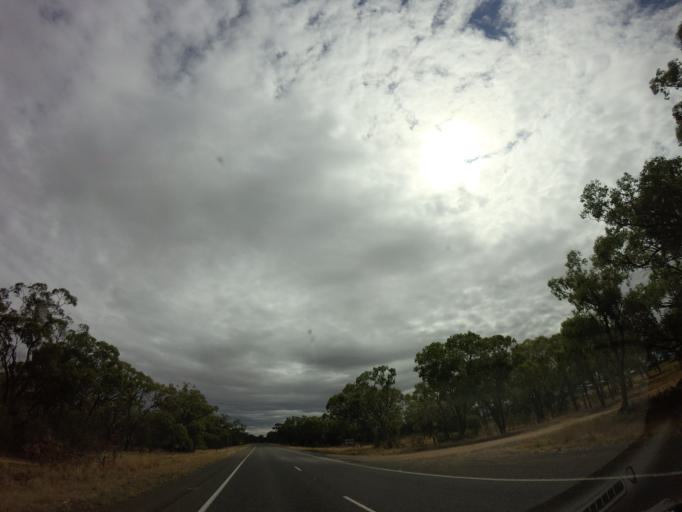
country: AU
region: New South Wales
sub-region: Narrabri
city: Narrabri
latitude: -30.3707
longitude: 149.7308
